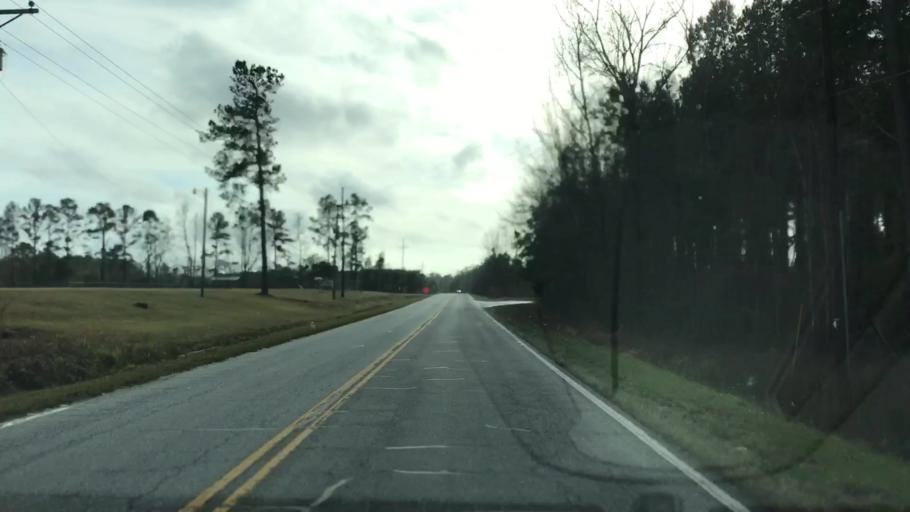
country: US
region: South Carolina
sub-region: Williamsburg County
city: Andrews
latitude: 33.3544
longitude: -79.6584
